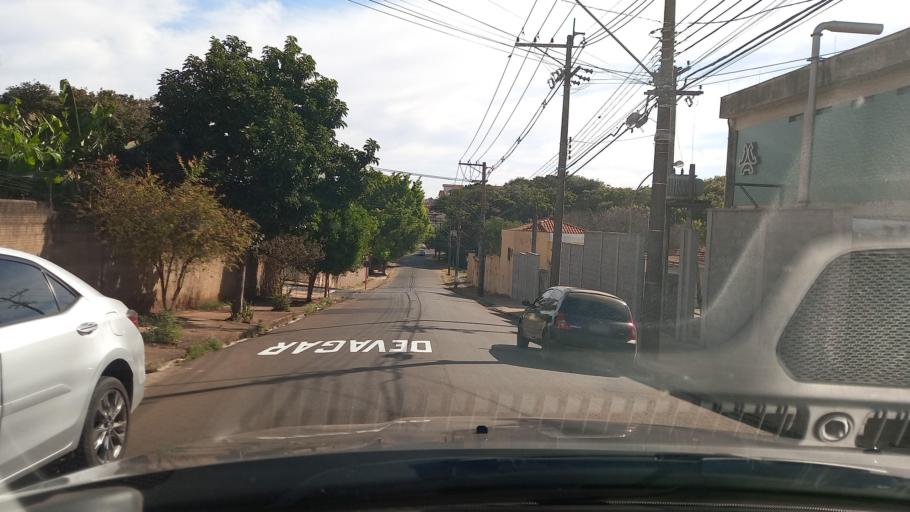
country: BR
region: Sao Paulo
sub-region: Sao Carlos
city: Sao Carlos
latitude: -21.9980
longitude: -47.8953
